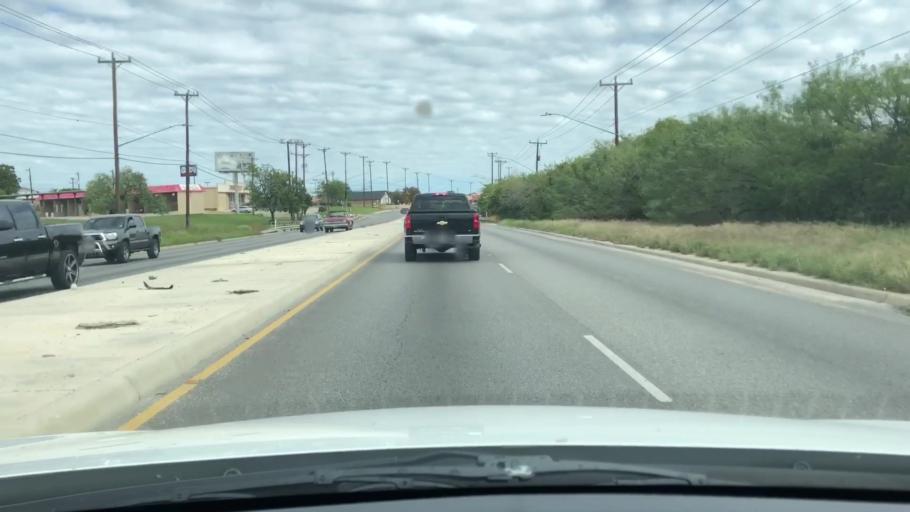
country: US
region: Texas
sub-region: Bexar County
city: Leon Valley
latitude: 29.4903
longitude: -98.6873
